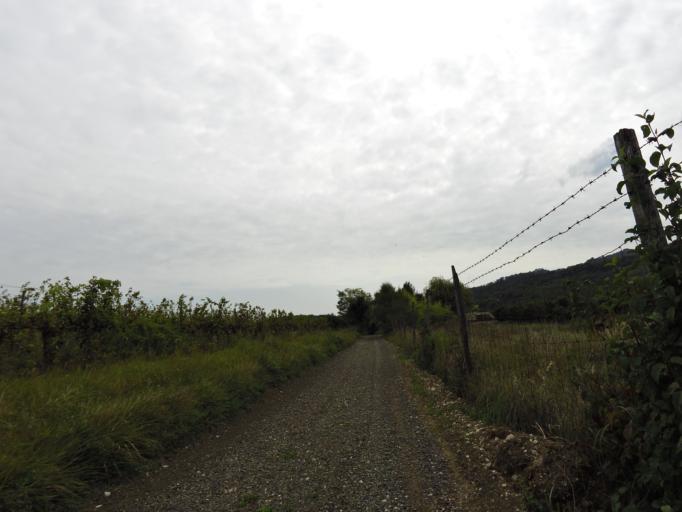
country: HU
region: Zala
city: Gyenesdias
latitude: 46.8472
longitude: 17.3364
